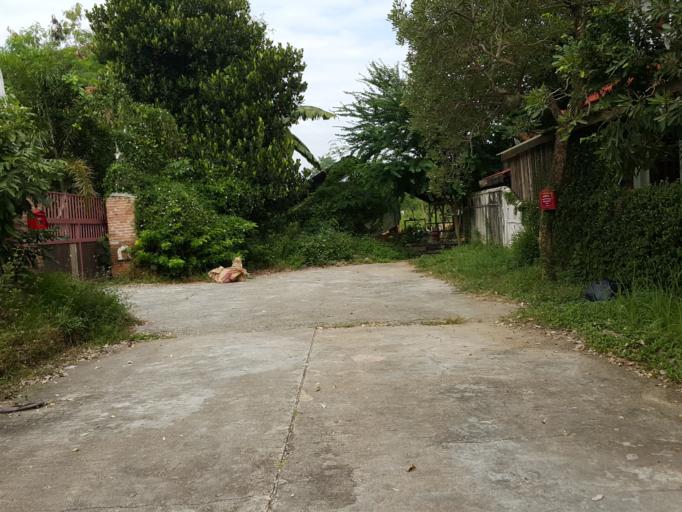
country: TH
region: Chiang Mai
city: San Kamphaeng
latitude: 18.7610
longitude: 99.0990
